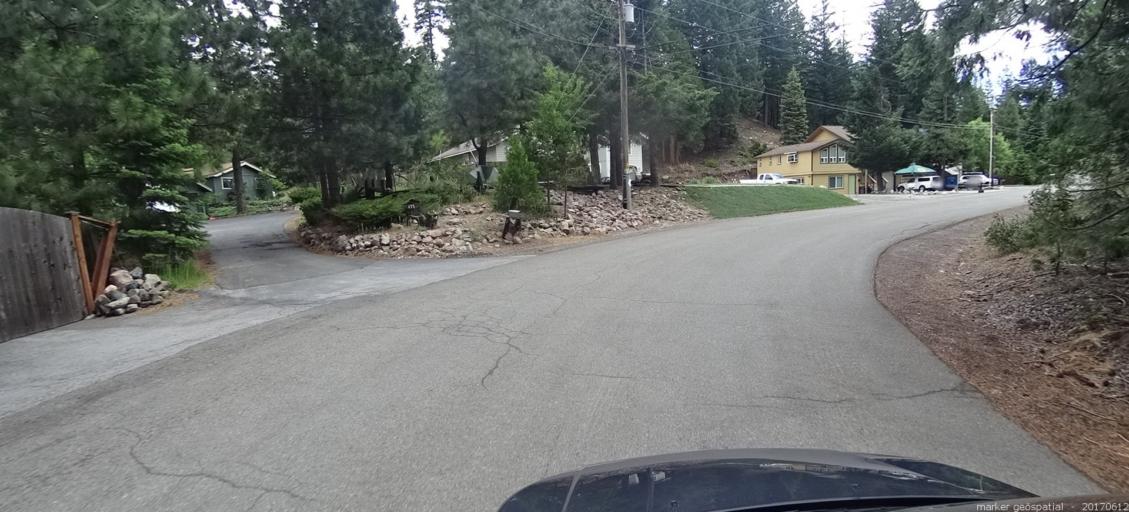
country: US
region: California
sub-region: Siskiyou County
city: Mount Shasta
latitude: 41.3466
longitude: -122.3567
